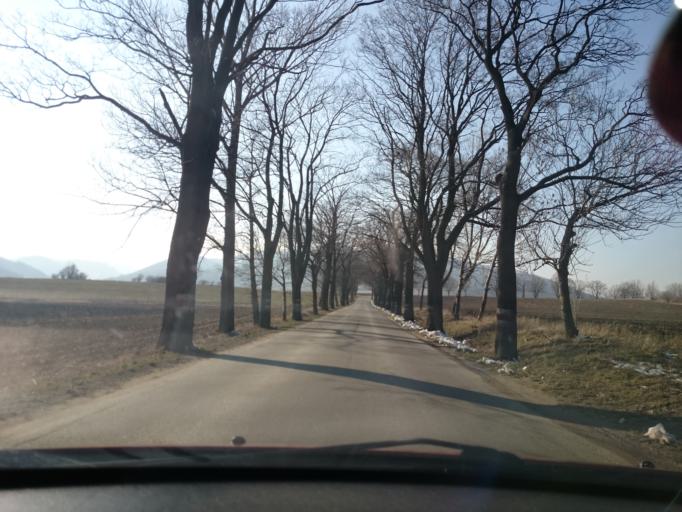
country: PL
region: Lower Silesian Voivodeship
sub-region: Powiat klodzki
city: Bystrzyca Klodzka
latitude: 50.3075
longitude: 16.6273
